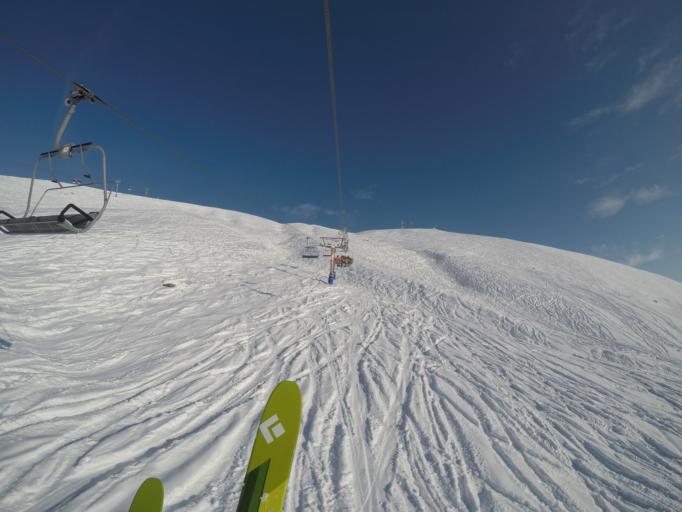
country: GE
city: Gudauri
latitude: 42.4834
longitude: 44.4952
